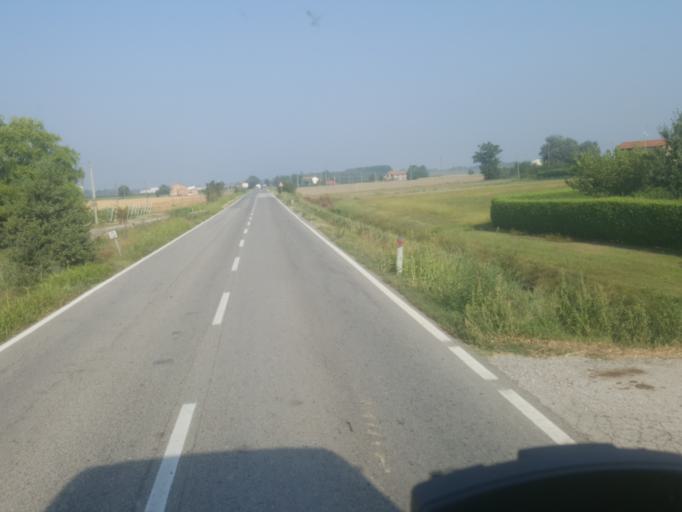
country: IT
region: Emilia-Romagna
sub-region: Provincia di Ravenna
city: Lavezzola
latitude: 44.5624
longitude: 11.9063
